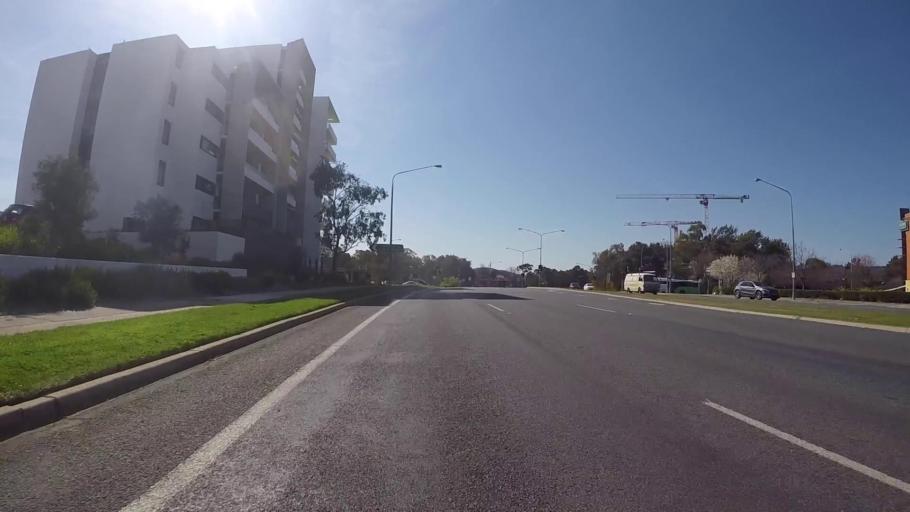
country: AU
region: Australian Capital Territory
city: Forrest
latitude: -35.3408
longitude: 149.0823
